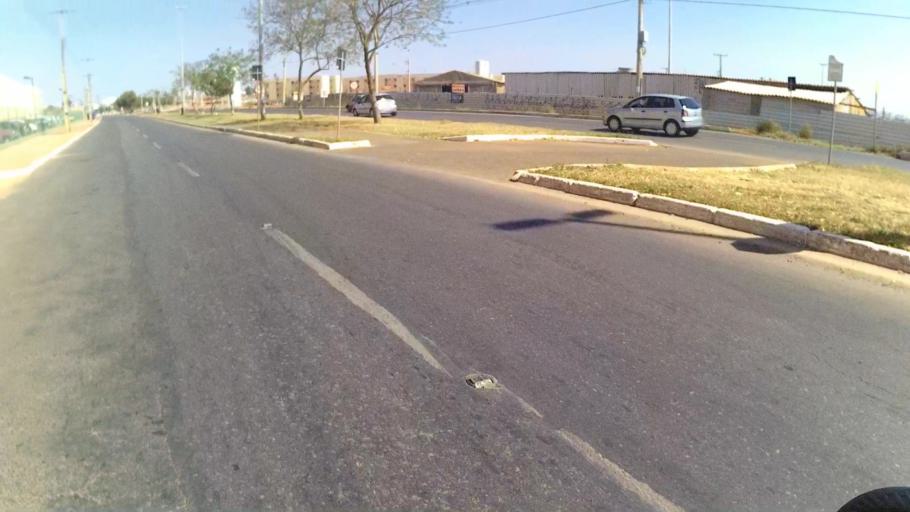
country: BR
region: Federal District
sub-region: Brasilia
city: Brasilia
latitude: -15.8921
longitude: -48.0475
